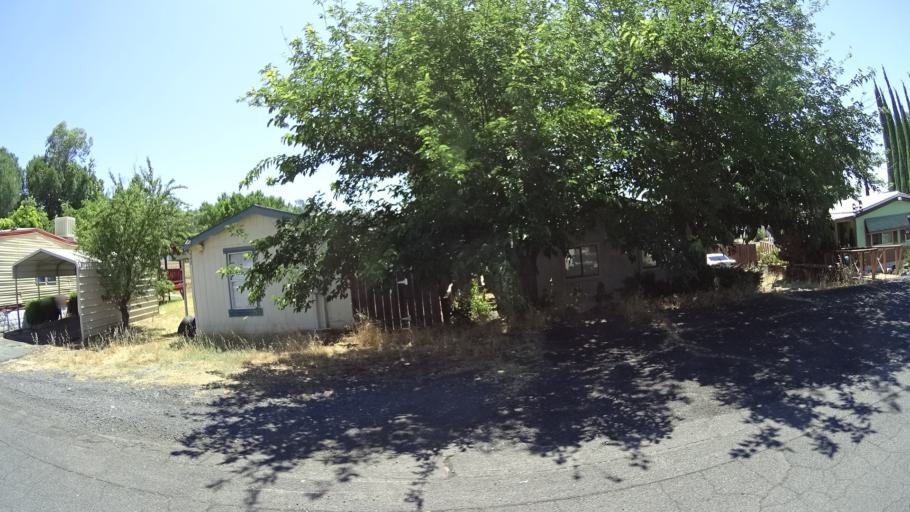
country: US
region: California
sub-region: Calaveras County
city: Copperopolis
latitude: 37.9413
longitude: -120.6067
